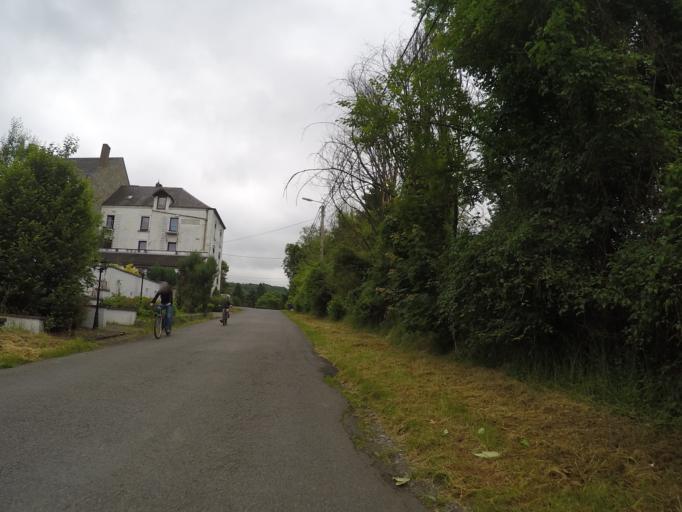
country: BE
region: Wallonia
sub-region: Province de Namur
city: Yvoir
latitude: 50.3366
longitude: 4.9271
